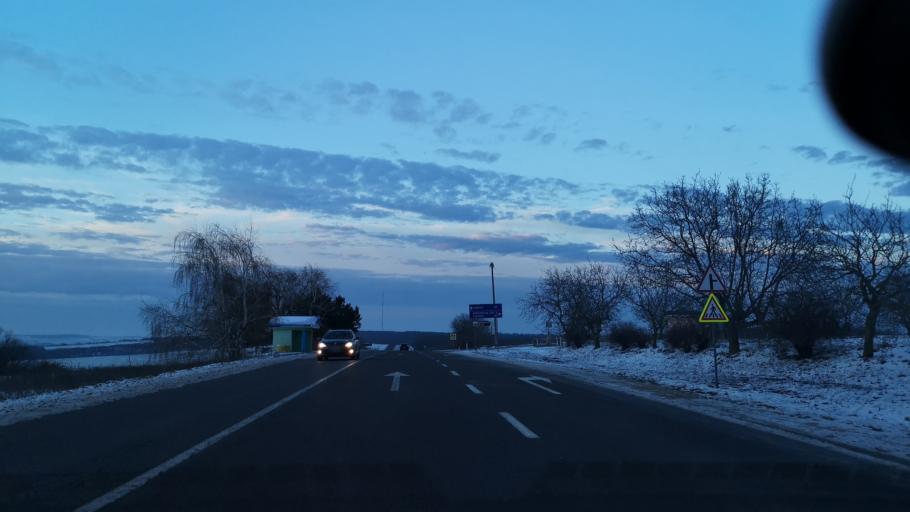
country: MD
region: Rezina
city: Saharna
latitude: 47.6332
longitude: 28.8371
